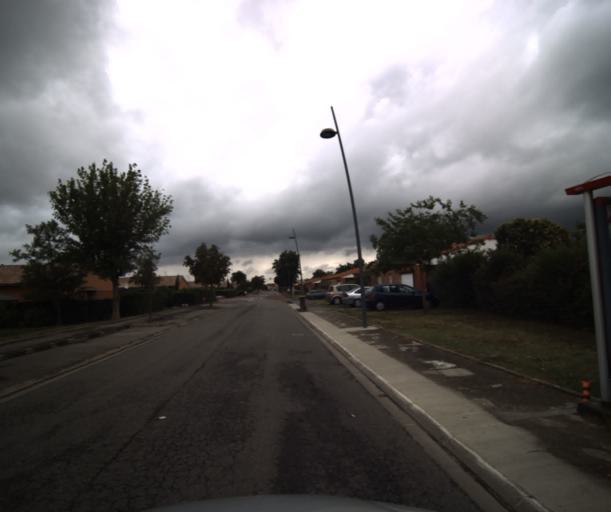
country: FR
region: Midi-Pyrenees
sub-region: Departement de la Haute-Garonne
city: Portet-sur-Garonne
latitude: 43.5402
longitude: 1.4099
